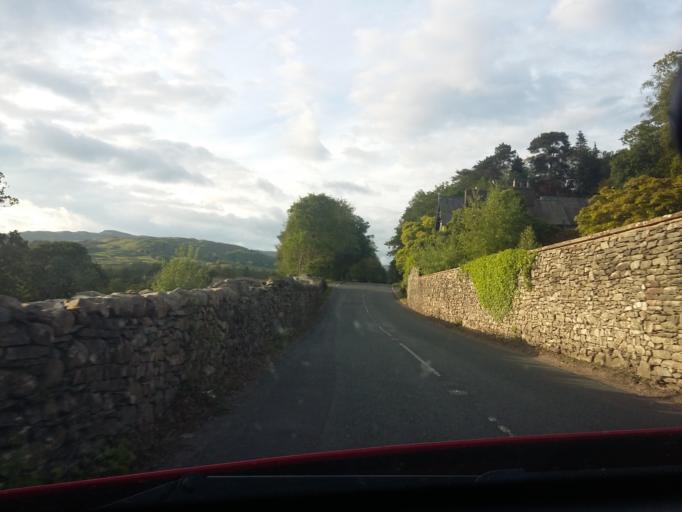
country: GB
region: England
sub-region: Cumbria
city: Windermere
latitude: 54.3946
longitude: -2.9152
